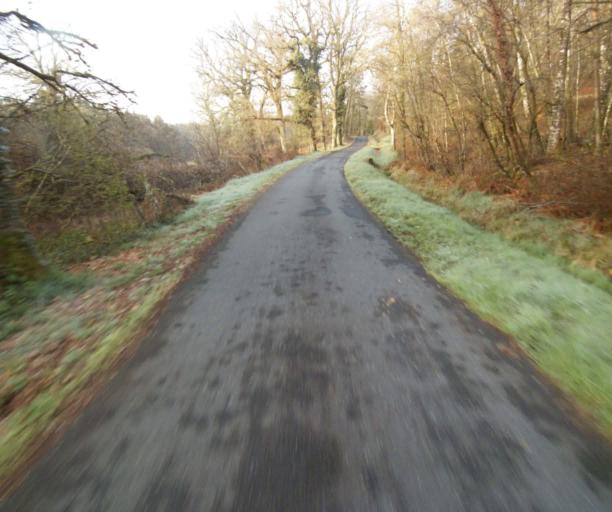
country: FR
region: Limousin
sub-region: Departement de la Correze
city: Correze
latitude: 45.3112
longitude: 1.8576
